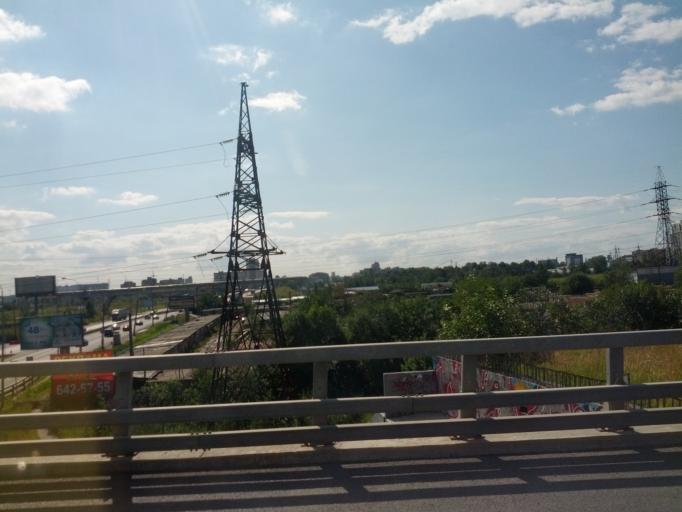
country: RU
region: Leningrad
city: Rybatskoye
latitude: 59.8878
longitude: 30.5052
